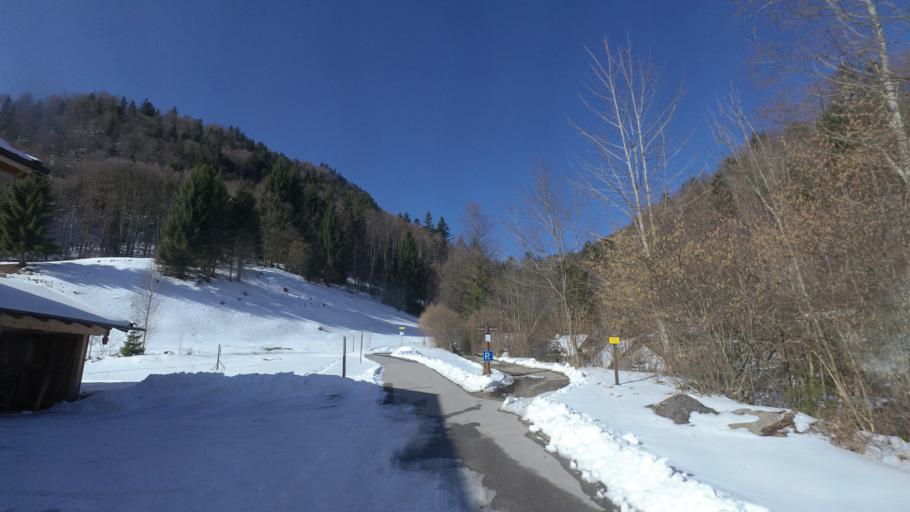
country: DE
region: Bavaria
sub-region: Upper Bavaria
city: Ruhpolding
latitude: 47.7450
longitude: 12.6119
